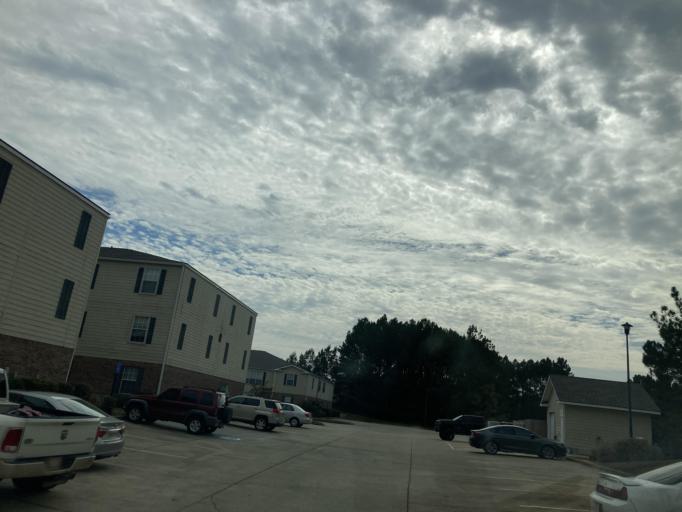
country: US
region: Mississippi
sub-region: Lamar County
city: West Hattiesburg
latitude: 31.3245
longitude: -89.4129
